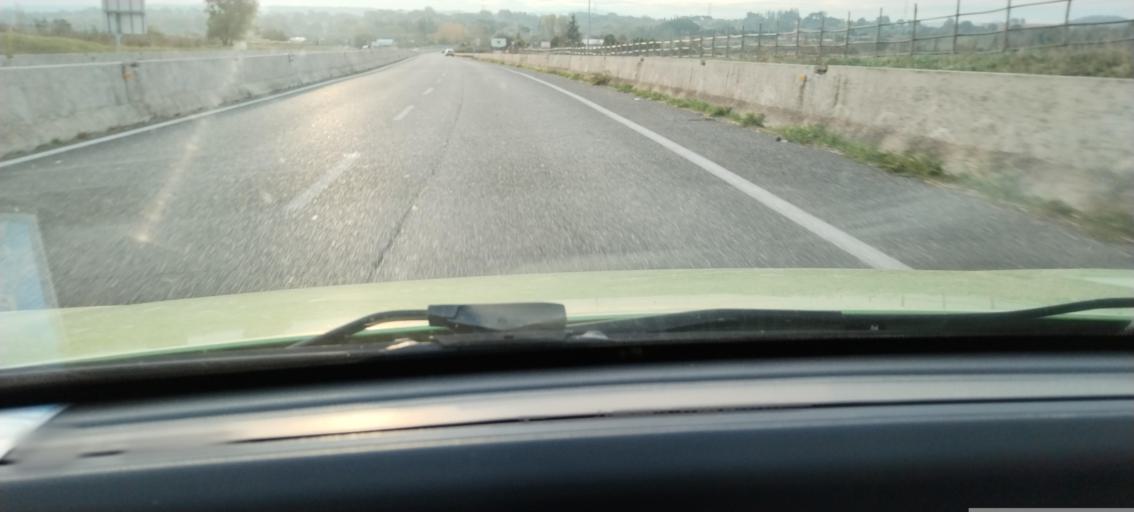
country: IT
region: Latium
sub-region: Provincia di Viterbo
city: Monterosi
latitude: 42.1917
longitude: 12.3154
